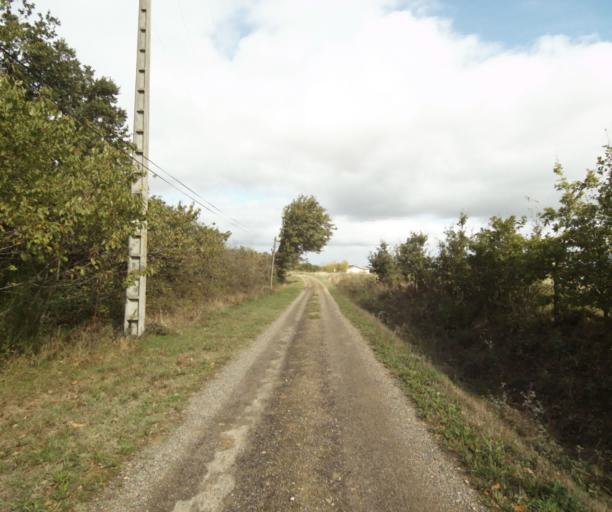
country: FR
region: Midi-Pyrenees
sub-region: Departement du Tarn-et-Garonne
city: Beaumont-de-Lomagne
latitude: 43.8820
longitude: 1.0751
